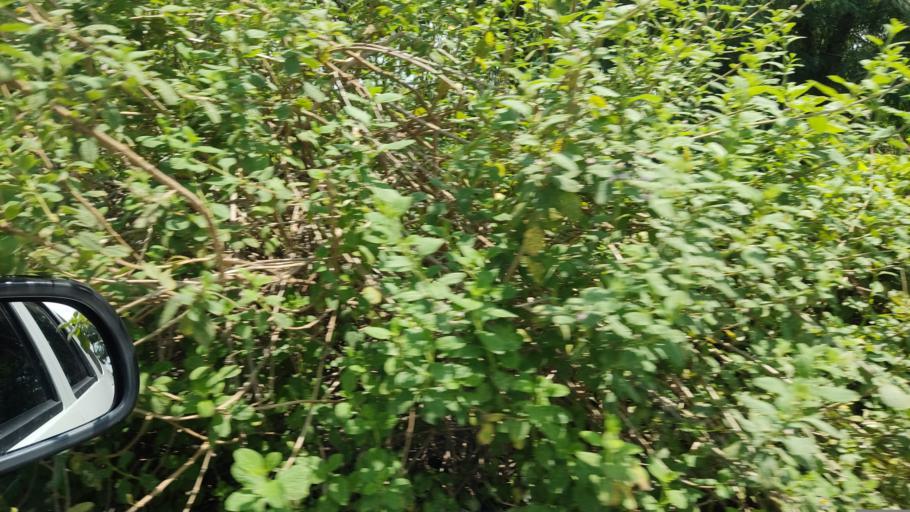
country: CO
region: Valle del Cauca
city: Cali
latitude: 3.4153
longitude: -76.5218
